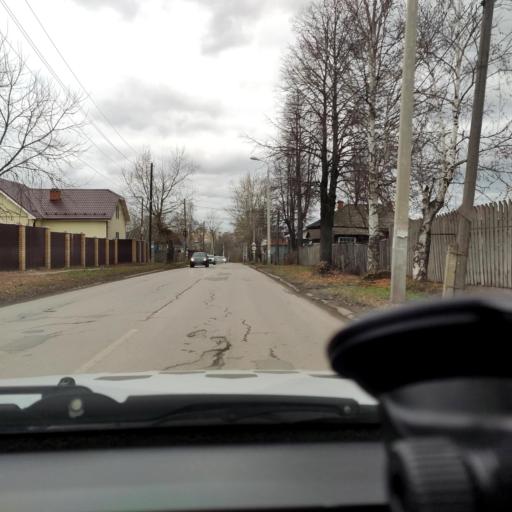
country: RU
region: Perm
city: Perm
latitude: 58.0193
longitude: 56.3149
